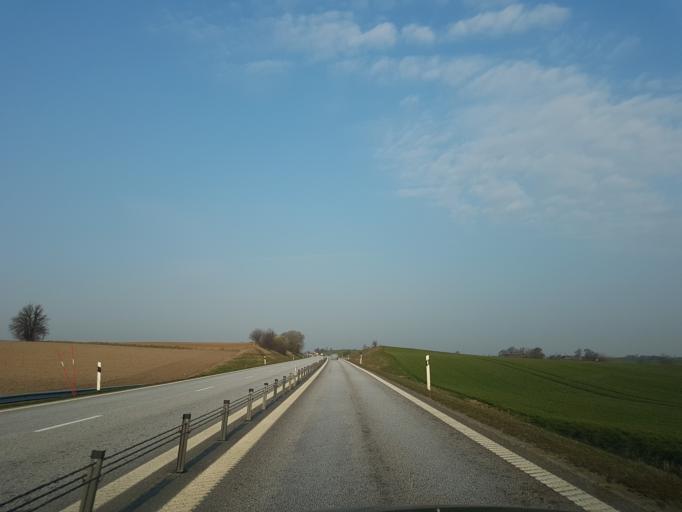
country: SE
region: Skane
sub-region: Skurups Kommun
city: Rydsgard
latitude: 55.4795
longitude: 13.6188
